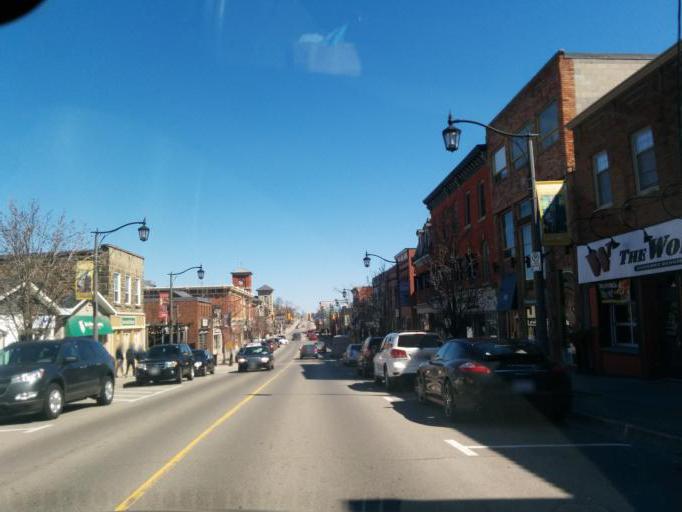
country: CA
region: Ontario
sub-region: Halton
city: Milton
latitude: 43.5125
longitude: -79.8838
